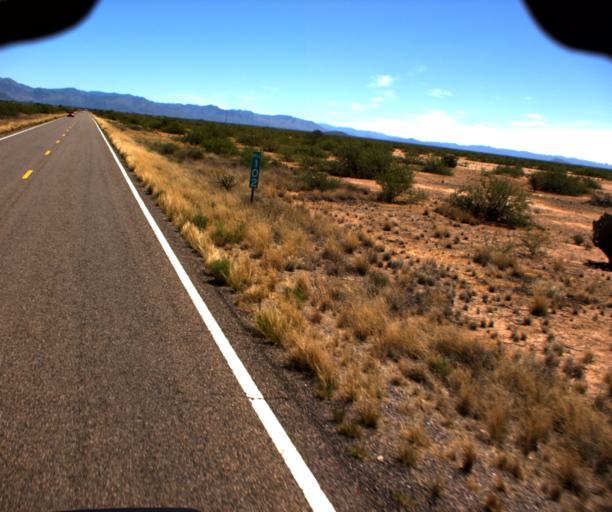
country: US
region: Arizona
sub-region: Yavapai County
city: Congress
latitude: 34.1176
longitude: -112.9651
